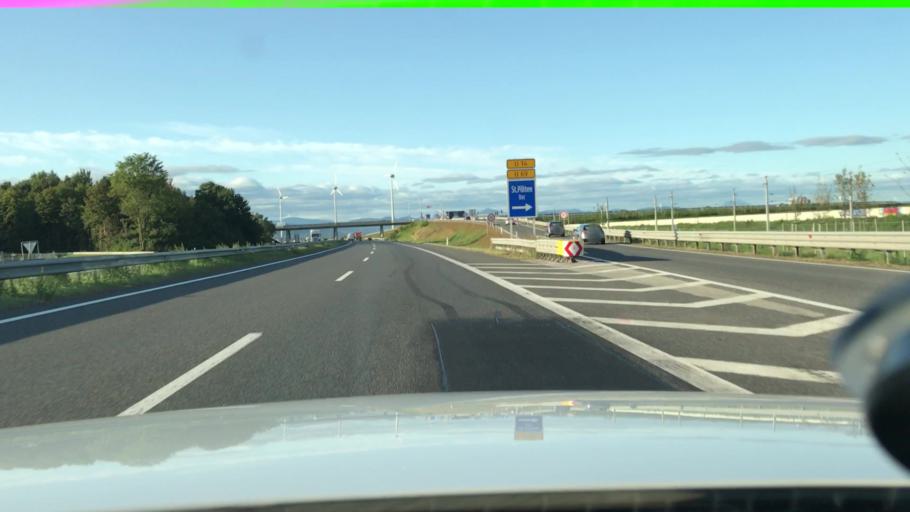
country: AT
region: Lower Austria
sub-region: Sankt Polten Stadt
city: Sankt Poelten
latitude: 48.2022
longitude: 15.6628
